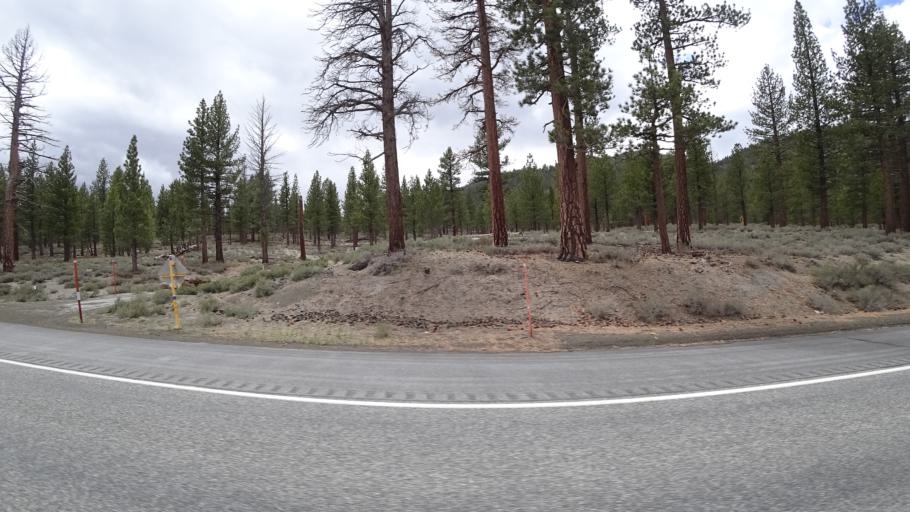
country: US
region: California
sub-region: Mono County
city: Mammoth Lakes
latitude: 37.7927
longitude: -119.0356
